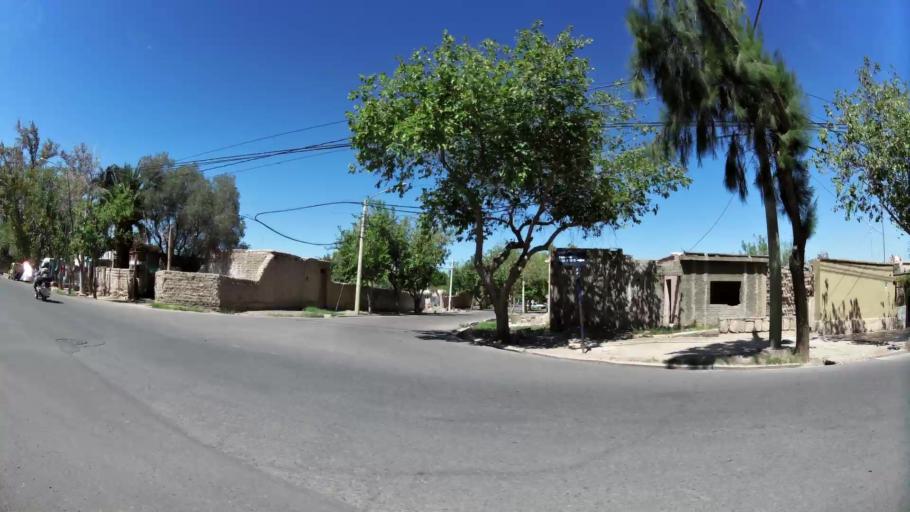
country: AR
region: San Juan
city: San Juan
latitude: -31.5231
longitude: -68.5409
